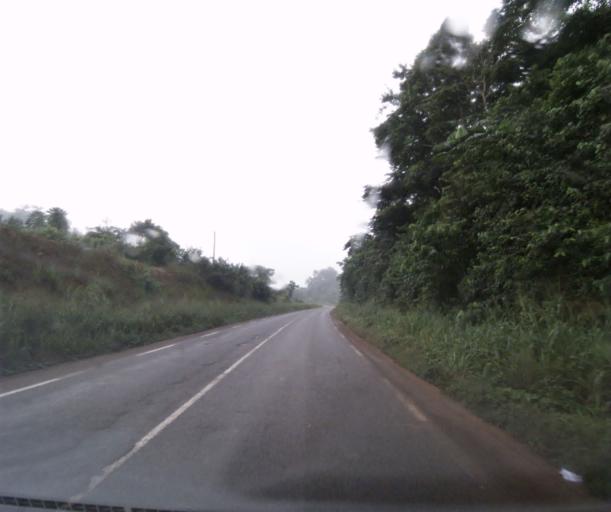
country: CM
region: Centre
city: Eseka
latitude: 3.8865
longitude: 10.7079
